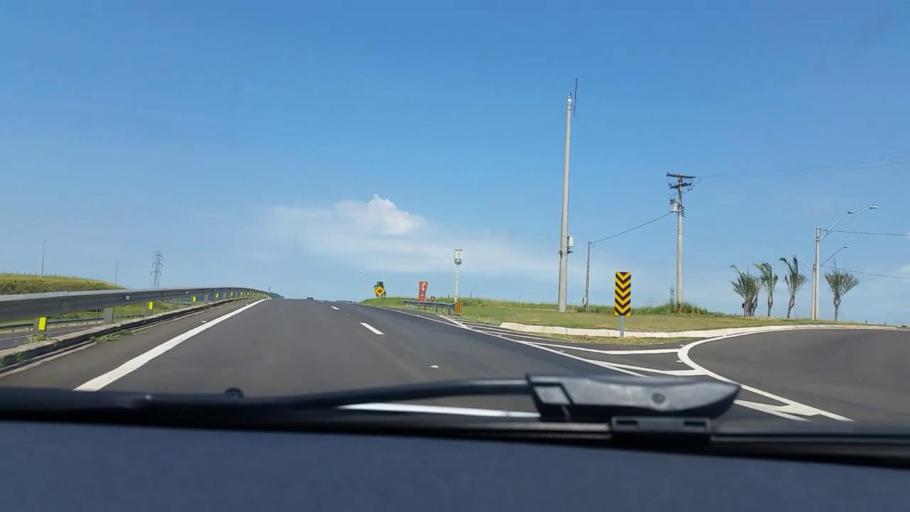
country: BR
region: Sao Paulo
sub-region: Bauru
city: Bauru
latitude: -22.3908
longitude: -49.0781
